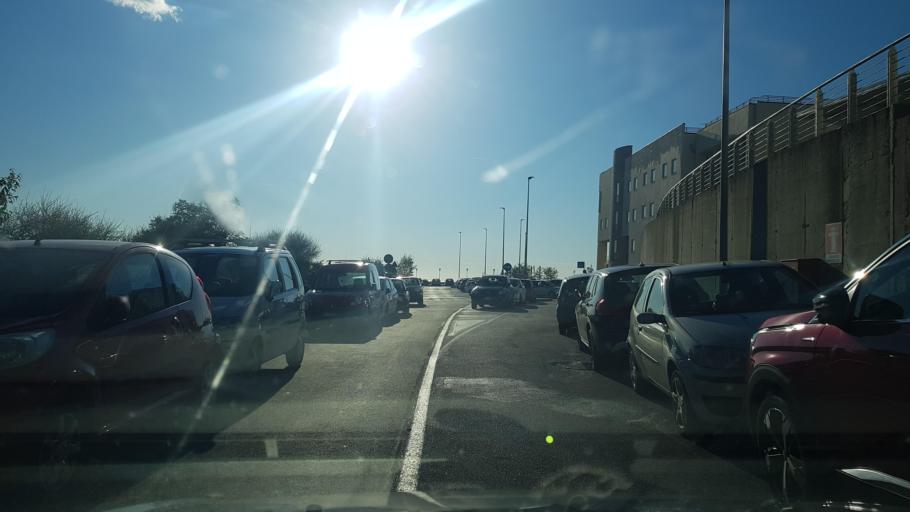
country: IT
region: Friuli Venezia Giulia
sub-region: Provincia di Trieste
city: Domio
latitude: 45.6328
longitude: 13.8272
